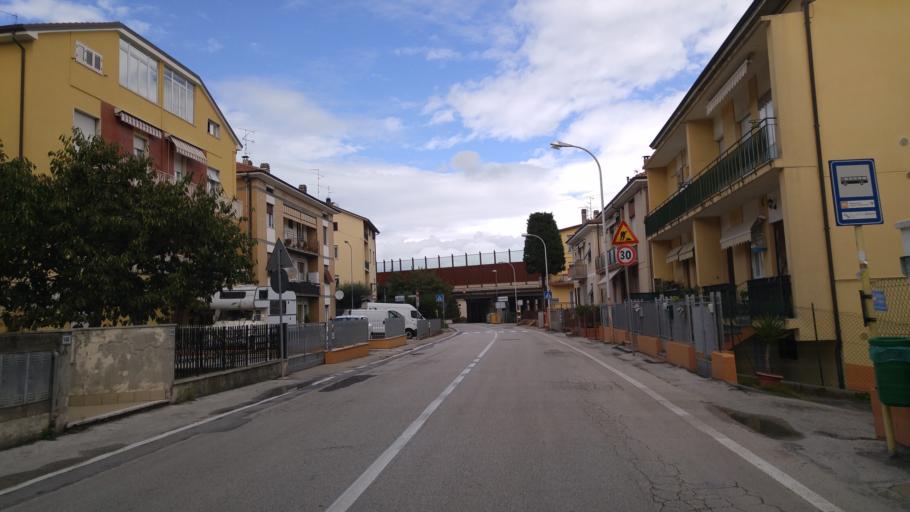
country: IT
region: The Marches
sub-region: Provincia di Pesaro e Urbino
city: Pesaro
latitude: 43.8836
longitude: 12.9018
